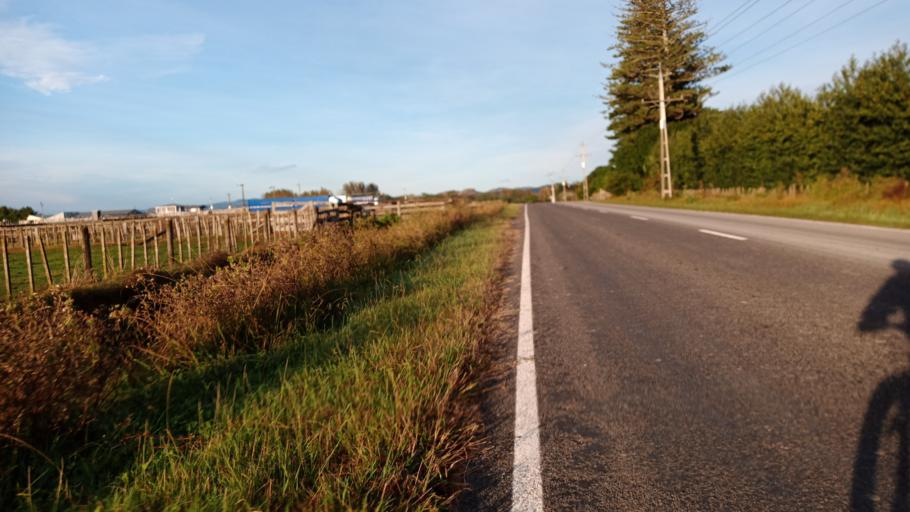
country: NZ
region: Gisborne
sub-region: Gisborne District
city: Gisborne
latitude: -38.6499
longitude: 177.9446
